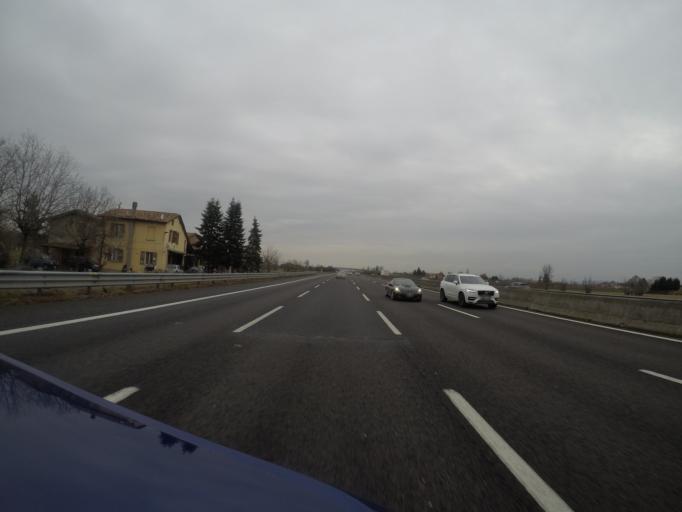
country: IT
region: Emilia-Romagna
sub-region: Provincia di Modena
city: San Cesario sul Panaro
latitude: 44.5725
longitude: 11.0074
